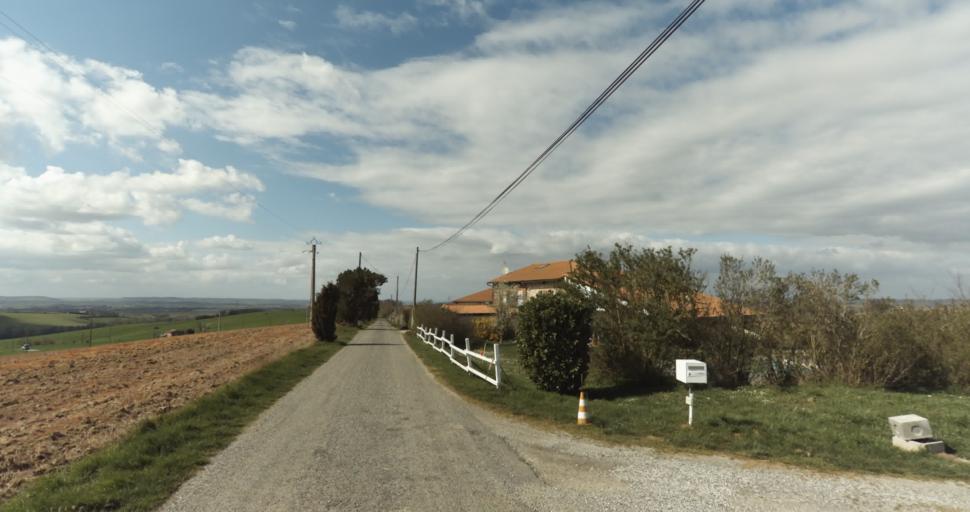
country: FR
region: Midi-Pyrenees
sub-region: Departement de la Haute-Garonne
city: Auterive
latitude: 43.3809
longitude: 1.4926
